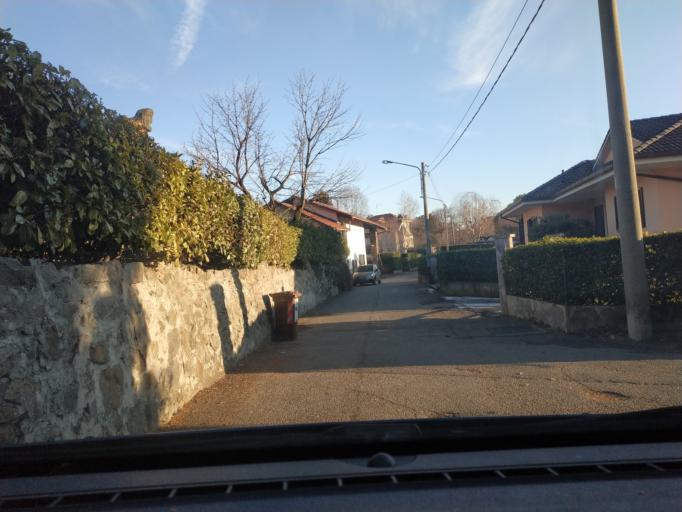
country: IT
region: Piedmont
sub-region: Provincia di Torino
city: Ivrea
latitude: 45.4699
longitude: 7.8636
